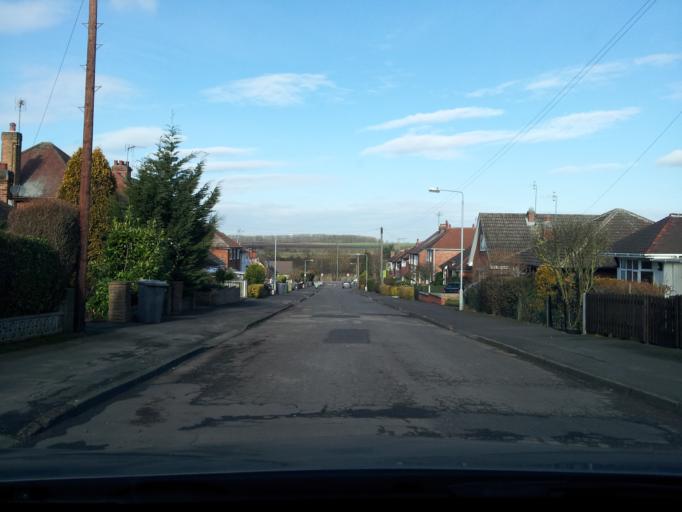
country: GB
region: England
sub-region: Nottinghamshire
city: Radcliffe on Trent
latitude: 52.9480
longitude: -1.0182
